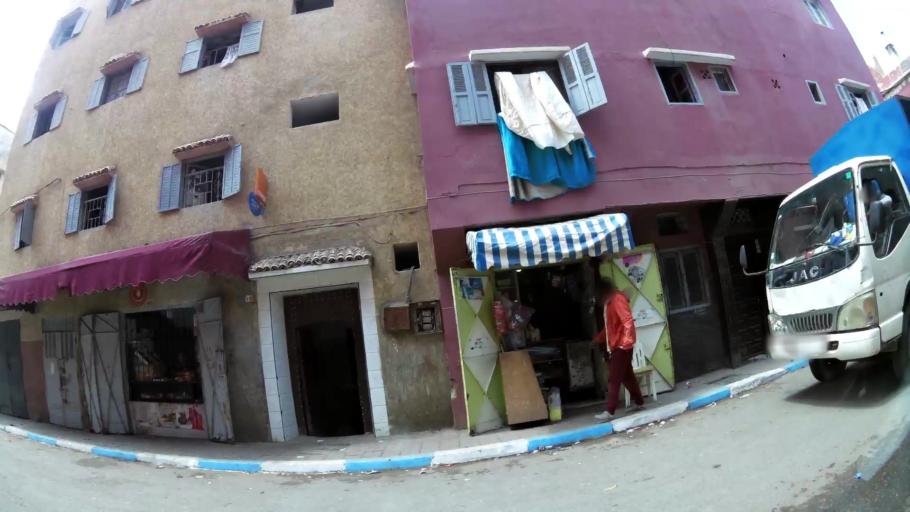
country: MA
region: Rabat-Sale-Zemmour-Zaer
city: Sale
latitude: 34.0533
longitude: -6.8219
